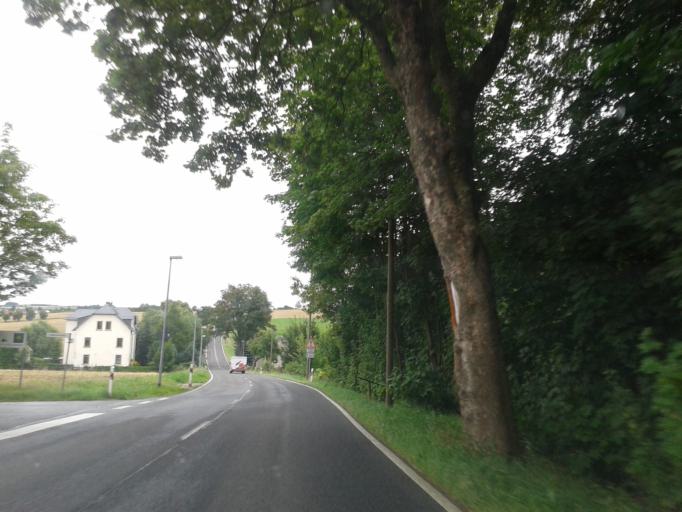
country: DE
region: Saxony
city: Tharandt
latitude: 50.9747
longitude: 13.5481
